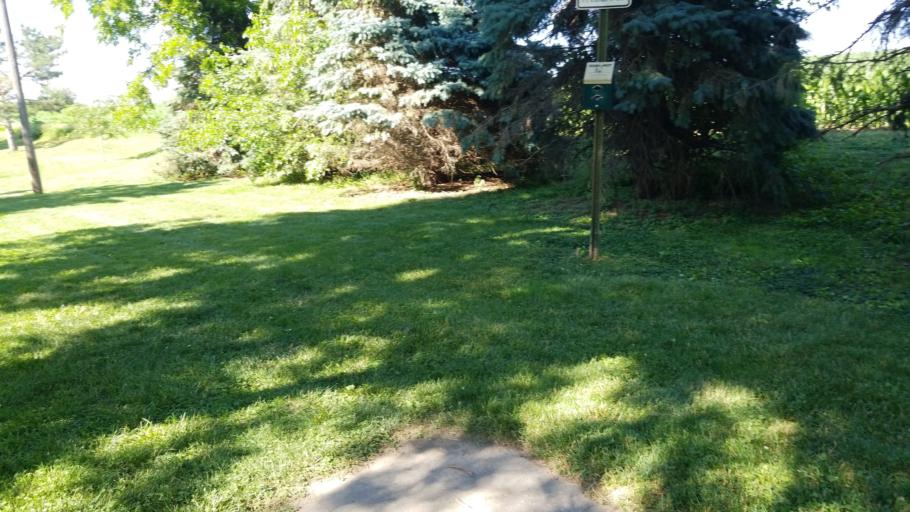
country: US
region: Nebraska
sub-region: Sarpy County
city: Papillion
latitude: 41.1415
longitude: -96.0191
